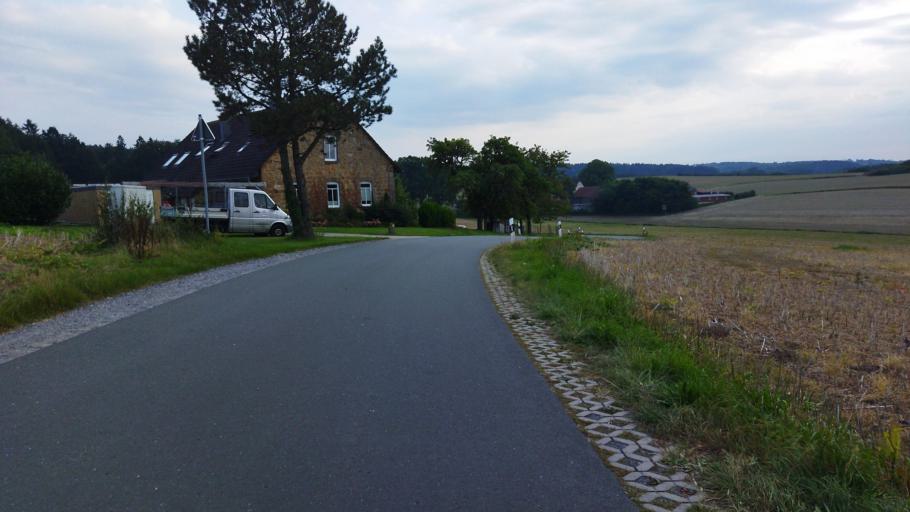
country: DE
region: Lower Saxony
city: Hagen
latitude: 52.1911
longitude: 8.0066
